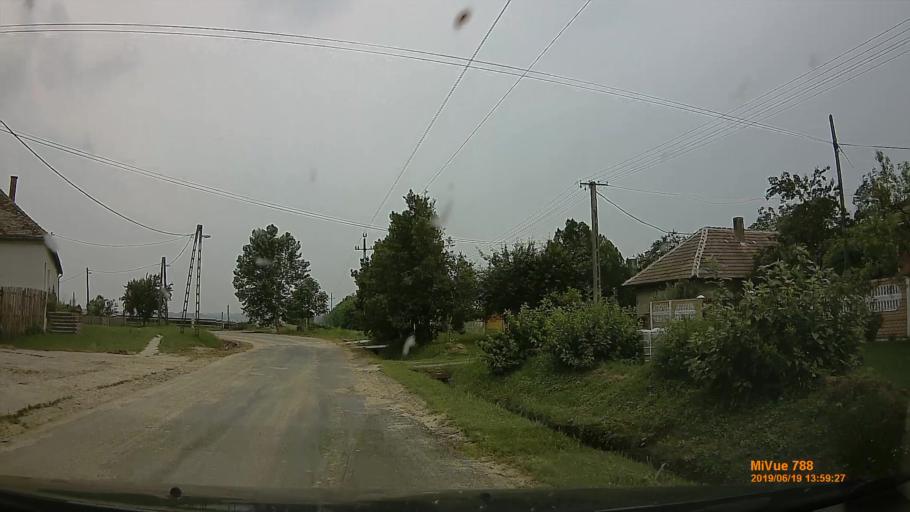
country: HU
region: Baranya
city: Szigetvar
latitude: 46.0881
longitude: 17.7978
